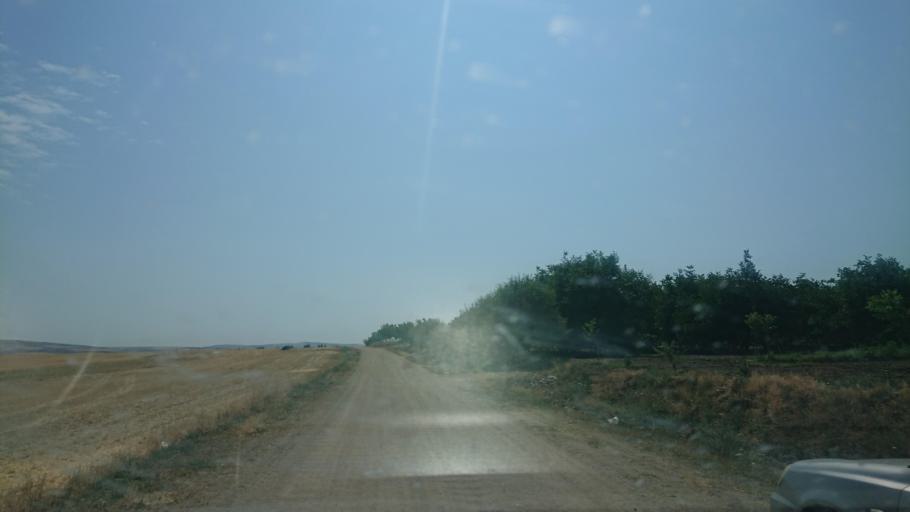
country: TR
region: Aksaray
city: Sariyahsi
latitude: 38.9571
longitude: 33.8974
